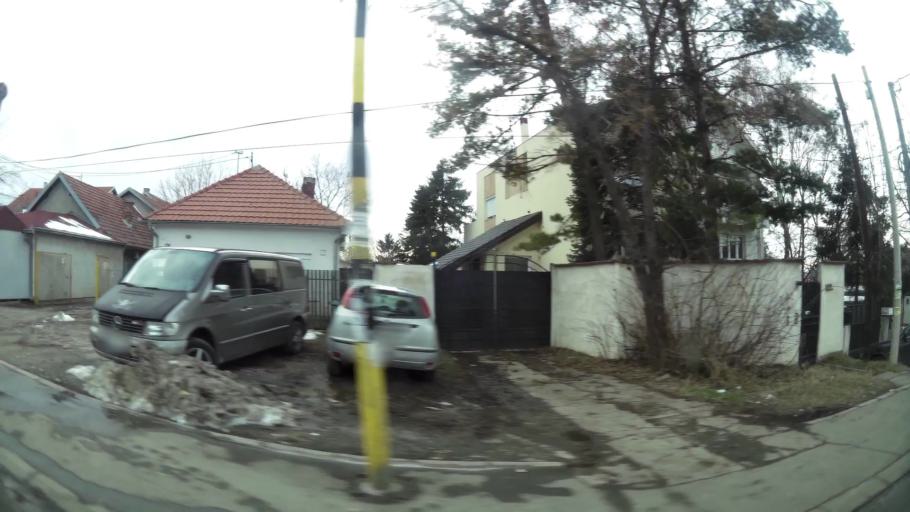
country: RS
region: Central Serbia
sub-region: Belgrade
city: Vozdovac
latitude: 44.7362
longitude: 20.4845
